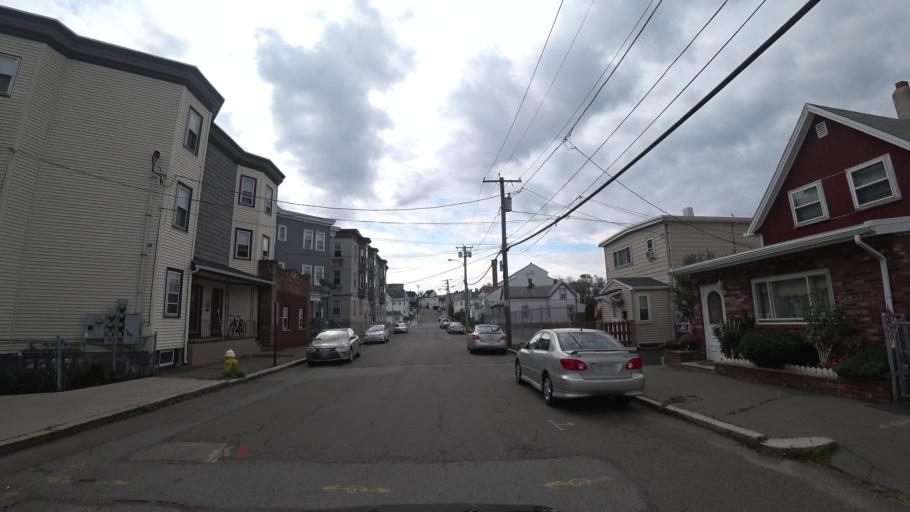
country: US
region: Massachusetts
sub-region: Suffolk County
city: Revere
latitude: 42.4000
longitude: -70.9901
